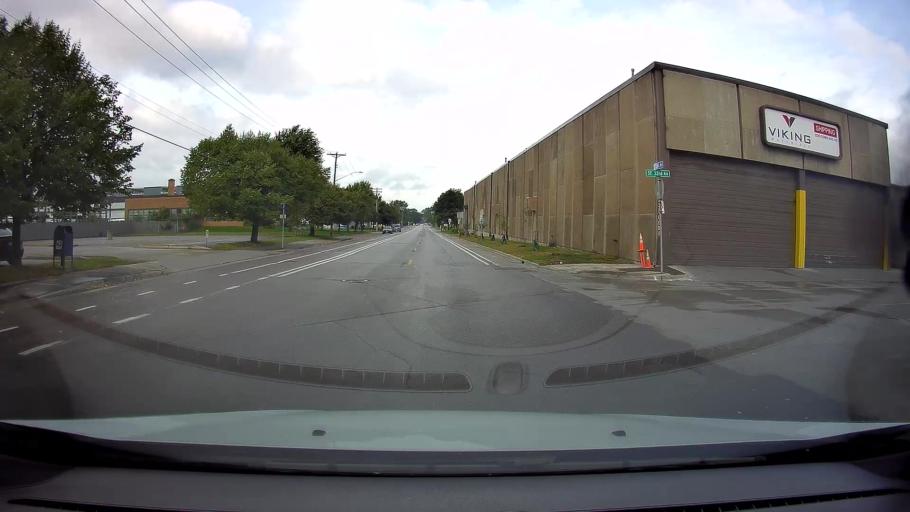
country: US
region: Minnesota
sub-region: Ramsey County
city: Lauderdale
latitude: 44.9881
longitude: -93.2078
